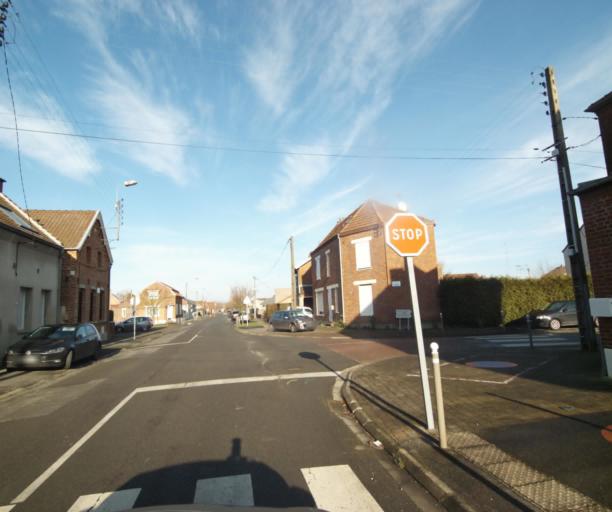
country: FR
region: Nord-Pas-de-Calais
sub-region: Departement du Nord
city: Maing
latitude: 50.3110
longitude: 3.4845
